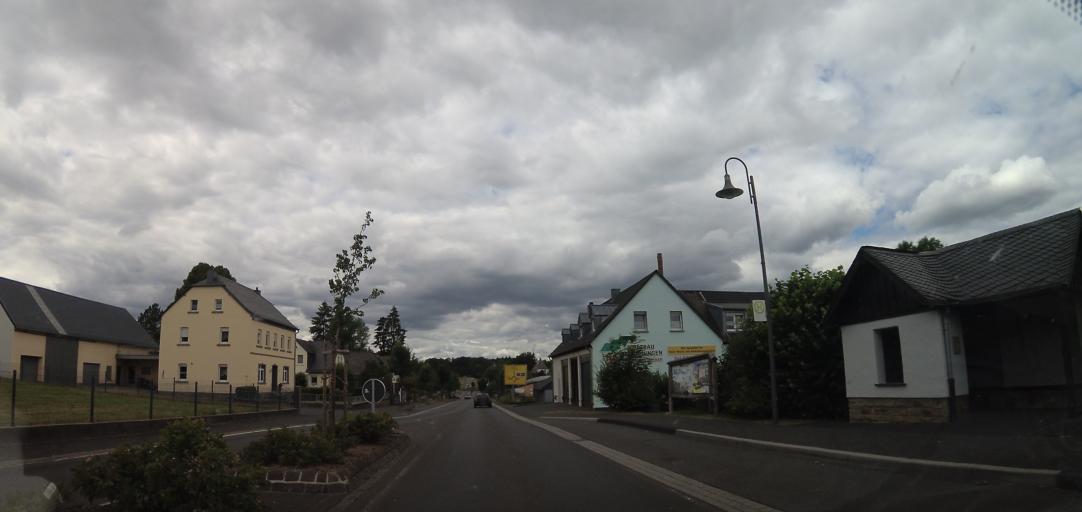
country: DE
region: Rheinland-Pfalz
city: Walsdorf
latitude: 50.2812
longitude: 6.7049
